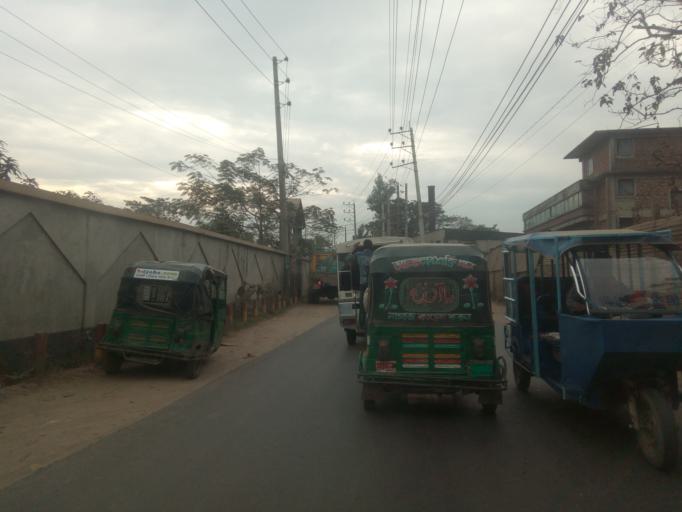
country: BD
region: Dhaka
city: Narayanganj
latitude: 23.5823
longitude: 90.5022
